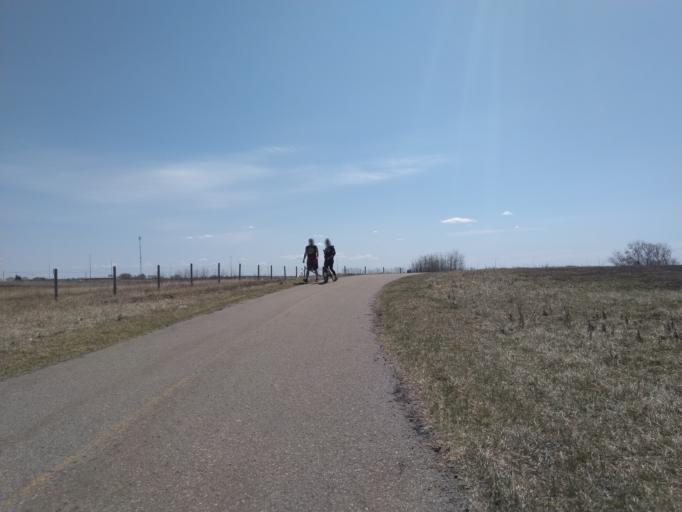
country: CA
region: Alberta
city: Chestermere
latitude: 51.0924
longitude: -113.9247
